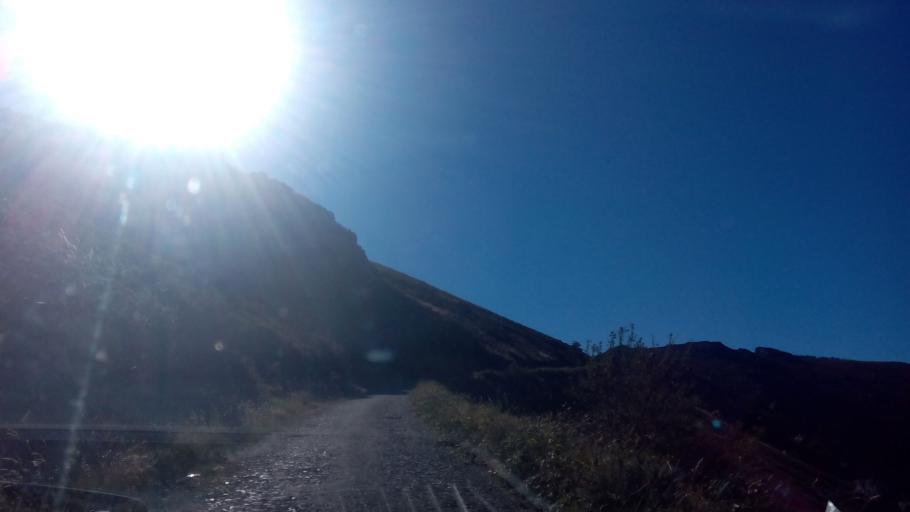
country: PT
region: Vila Real
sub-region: Mesao Frio
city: Mesao Frio
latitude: 41.2671
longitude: -7.9057
